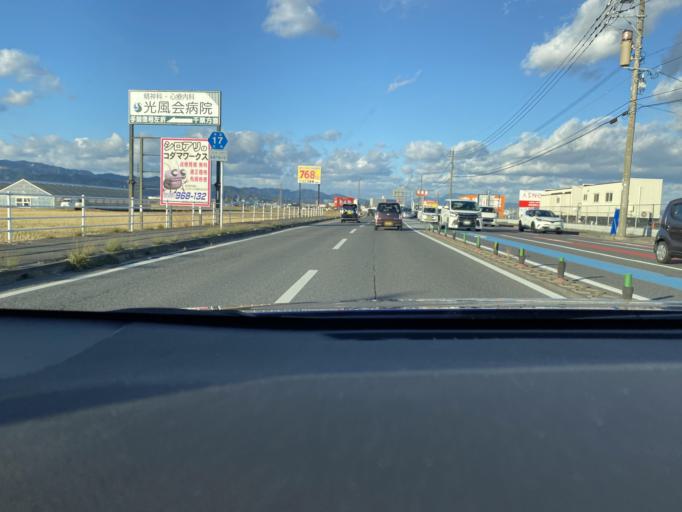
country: JP
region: Saga Prefecture
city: Tosu
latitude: 33.3483
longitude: 130.5145
